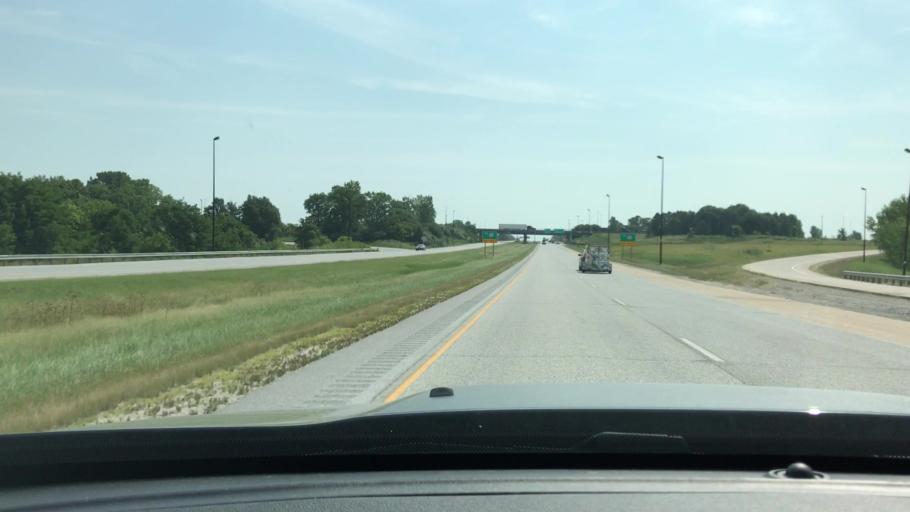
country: US
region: Illinois
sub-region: Henry County
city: Green Rock
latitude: 41.4404
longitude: -90.3364
